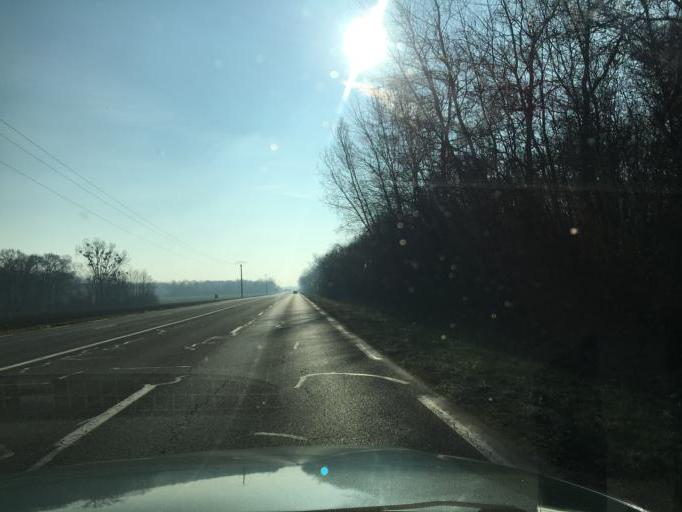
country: FR
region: Centre
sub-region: Departement du Loiret
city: Chevilly
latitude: 48.0095
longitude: 1.8787
